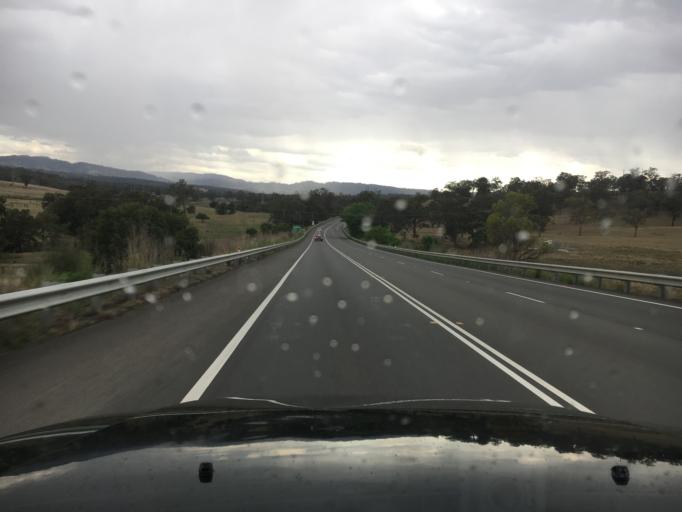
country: AU
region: New South Wales
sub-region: Muswellbrook
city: Muswellbrook
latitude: -32.2851
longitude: 150.9195
